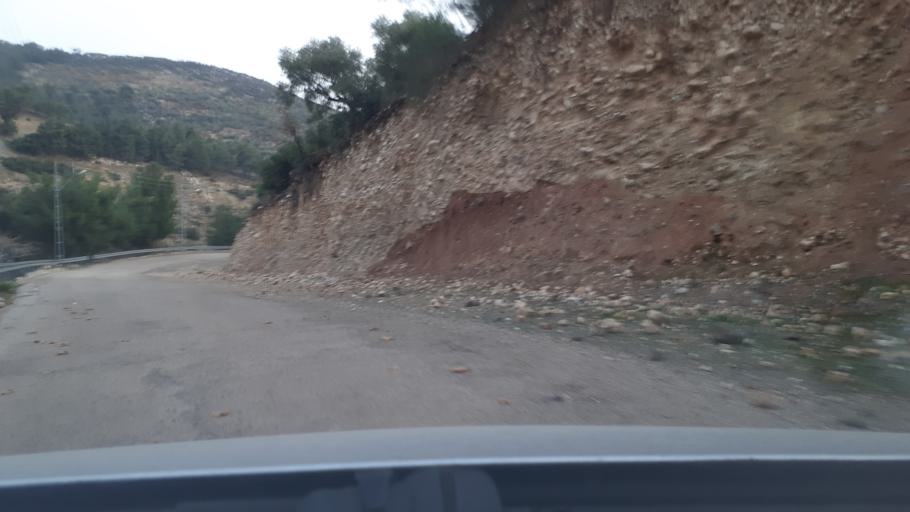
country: TR
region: Hatay
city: Kirikhan
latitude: 36.5306
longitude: 36.3157
